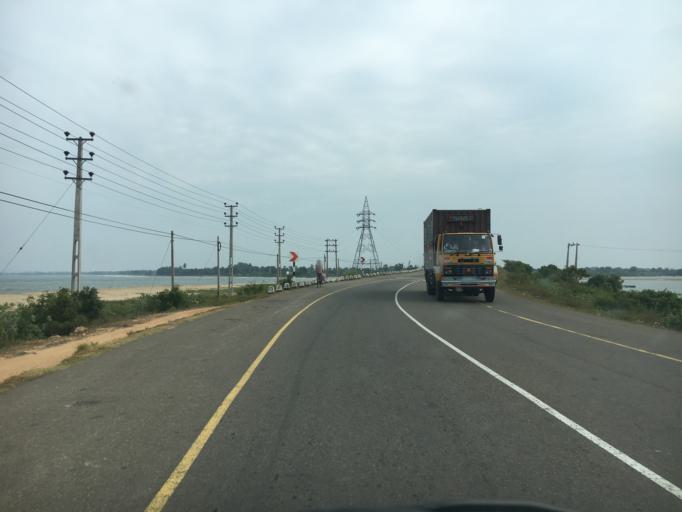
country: LK
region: Eastern Province
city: Trincomalee
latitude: 8.4731
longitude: 81.2013
